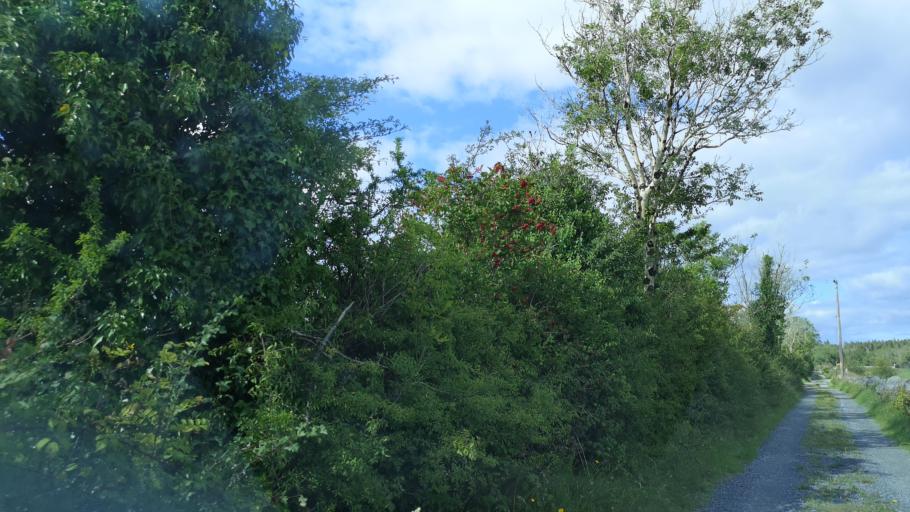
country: IE
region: Connaught
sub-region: County Galway
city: Moycullen
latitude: 53.3554
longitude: -9.1576
